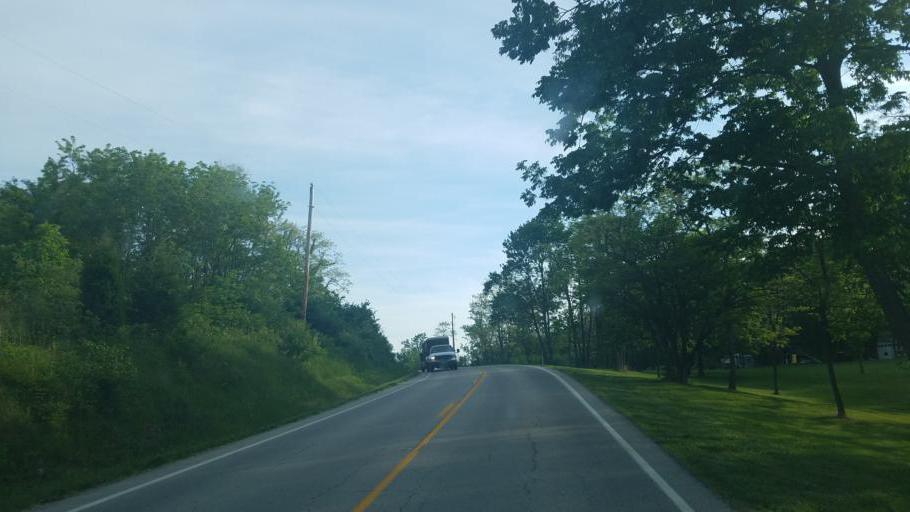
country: US
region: Ohio
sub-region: Ross County
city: Frankfort
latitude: 39.4113
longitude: -83.2784
